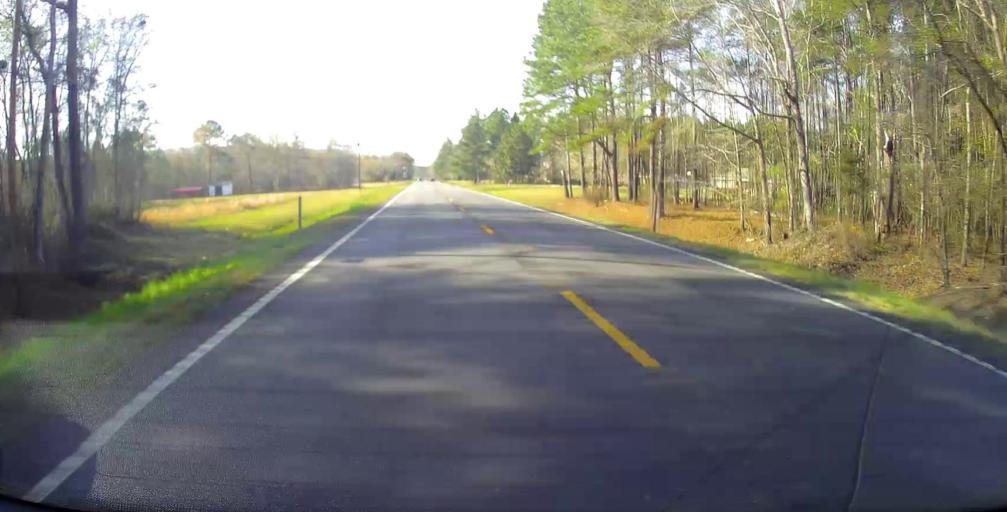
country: US
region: Georgia
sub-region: Montgomery County
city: Mount Vernon
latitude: 32.1842
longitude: -82.6068
